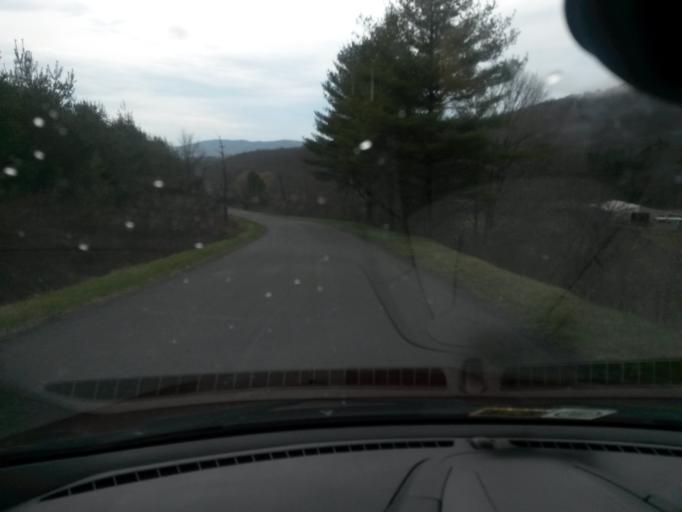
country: US
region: Virginia
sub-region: Bath County
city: Warm Springs
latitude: 38.0859
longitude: -79.7895
